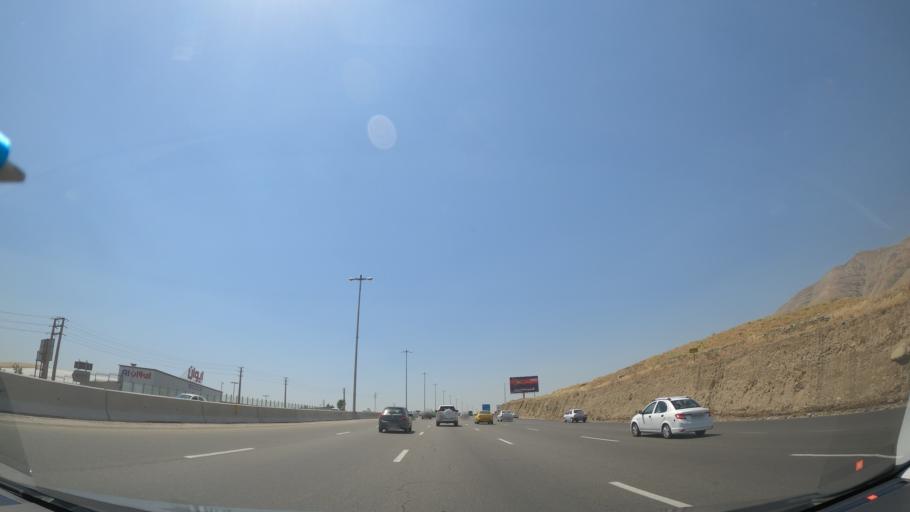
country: IR
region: Tehran
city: Shahr-e Qods
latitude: 35.7467
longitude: 51.0877
